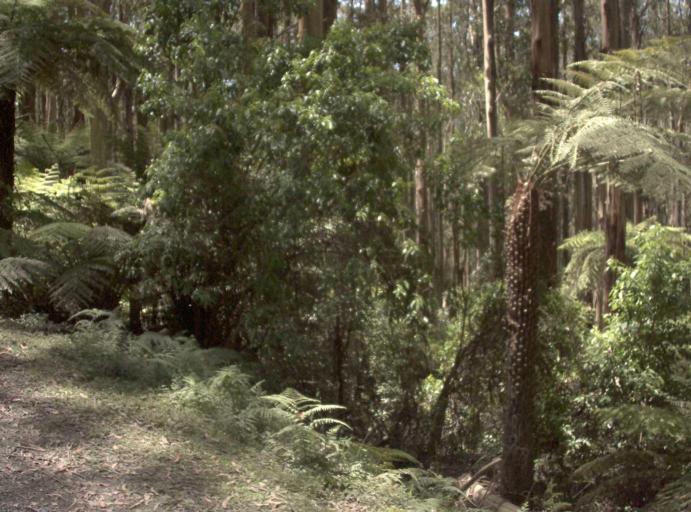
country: AU
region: Victoria
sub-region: Yarra Ranges
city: Millgrove
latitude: -37.7021
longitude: 145.7225
